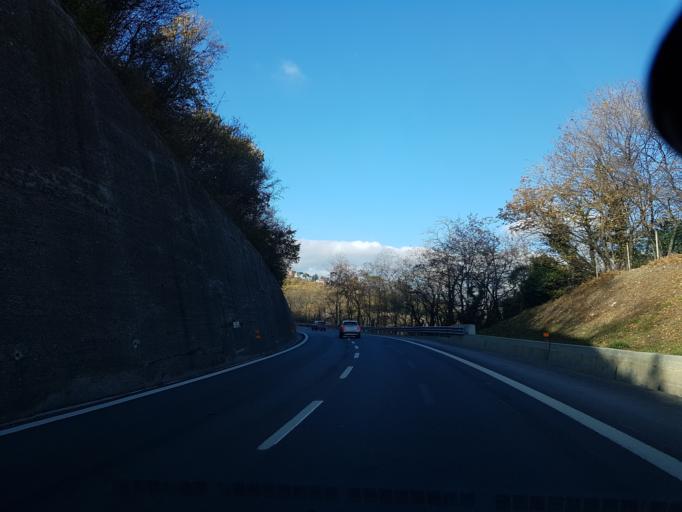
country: IT
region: Liguria
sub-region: Provincia di Genova
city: Manesseno
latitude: 44.4843
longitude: 8.9187
